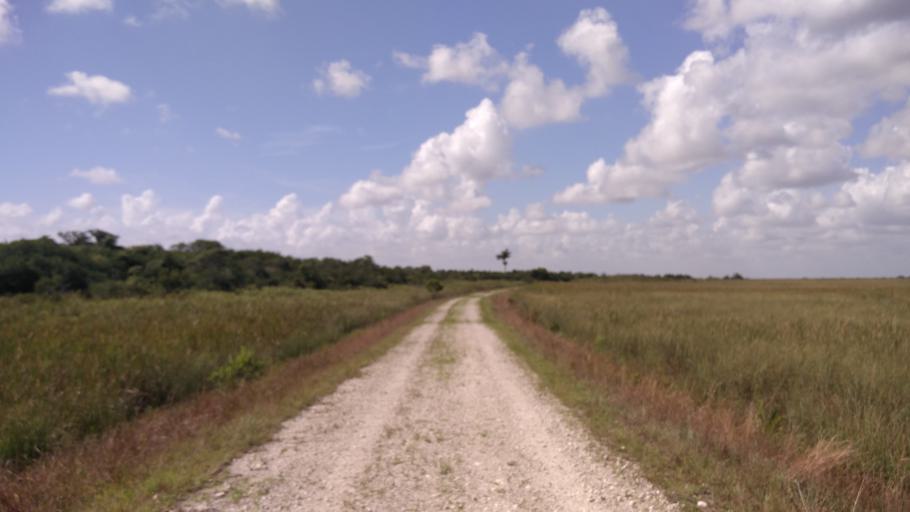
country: US
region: Florida
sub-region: Broward County
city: Weston
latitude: 26.0529
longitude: -80.4619
